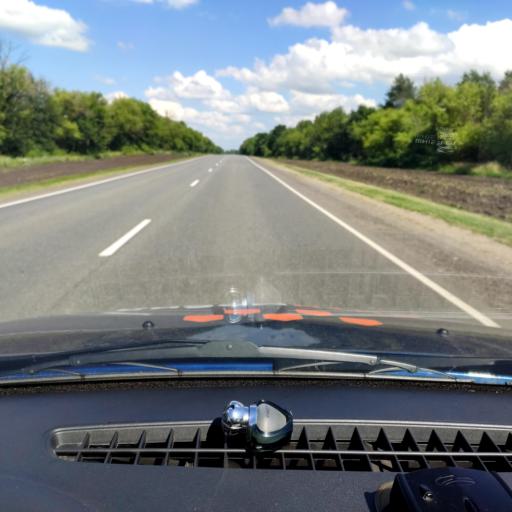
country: RU
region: Orjol
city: Livny
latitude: 52.4309
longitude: 37.8039
